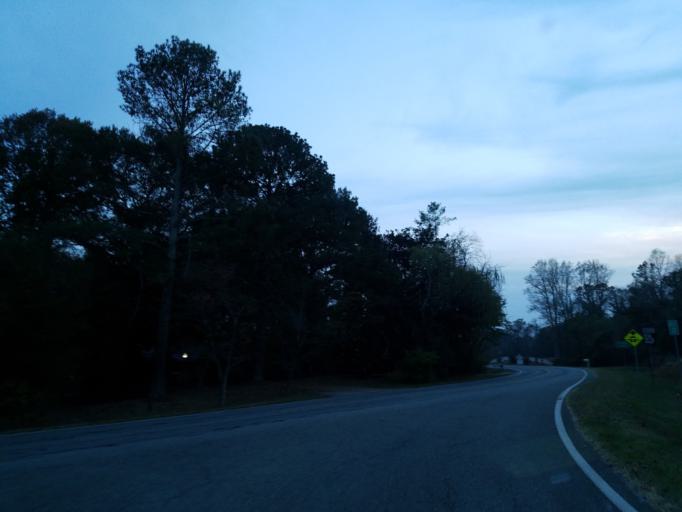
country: US
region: Georgia
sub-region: Pickens County
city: Jasper
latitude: 34.5106
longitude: -84.5577
